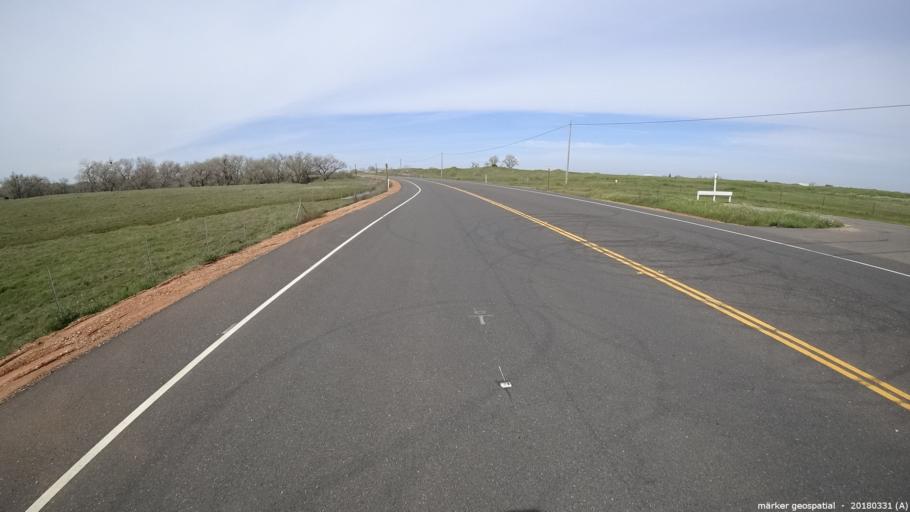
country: US
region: California
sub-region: Sacramento County
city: Gold River
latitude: 38.5954
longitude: -121.1810
